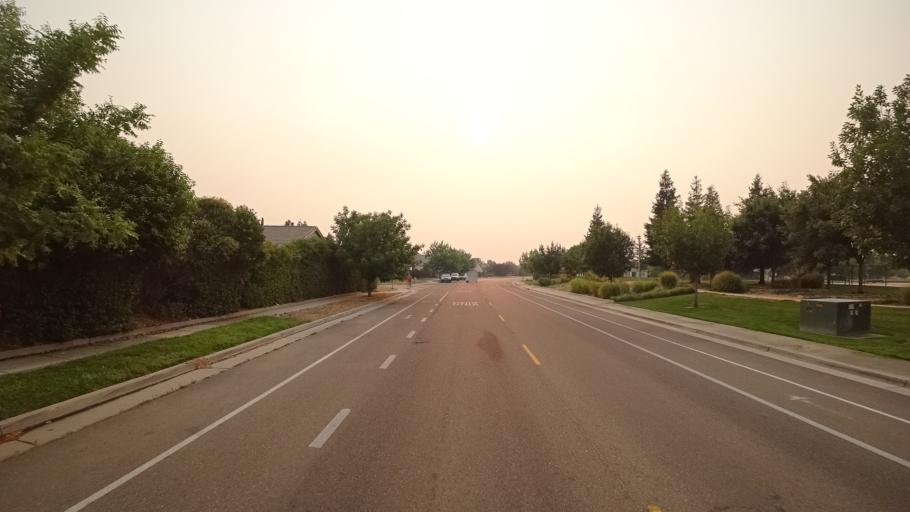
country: US
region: California
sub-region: Sacramento County
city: Laguna
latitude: 38.3996
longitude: -121.4354
